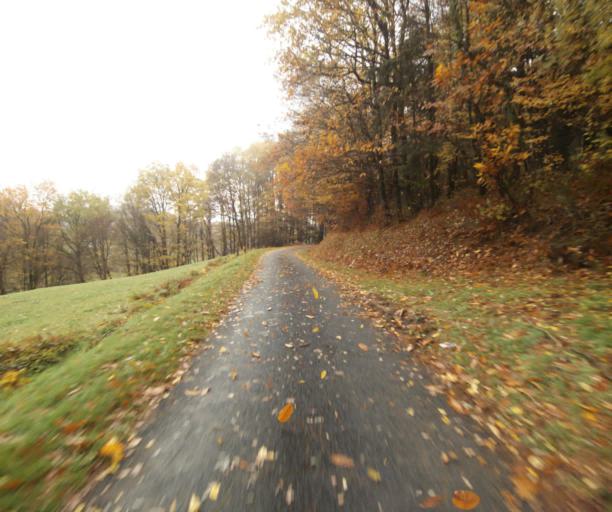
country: FR
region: Limousin
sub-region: Departement de la Correze
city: Cornil
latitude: 45.1952
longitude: 1.6345
